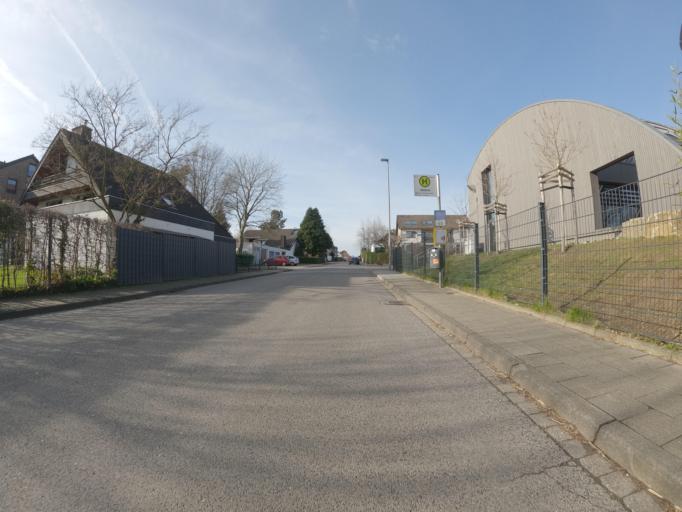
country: DE
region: North Rhine-Westphalia
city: Stolberg
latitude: 50.7426
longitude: 6.1625
